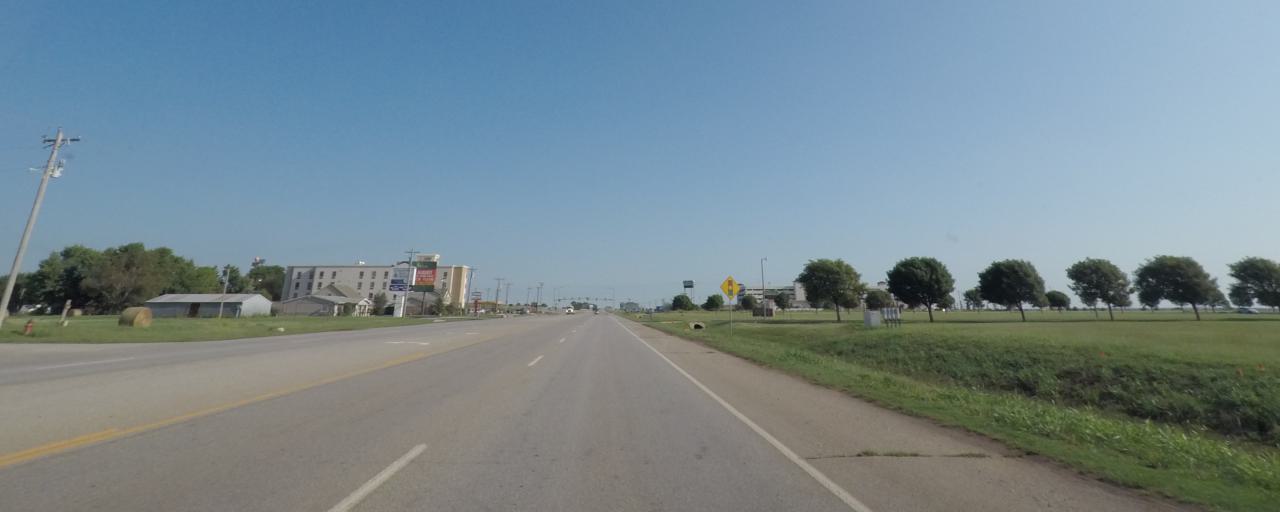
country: US
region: Oklahoma
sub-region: McClain County
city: Newcastle
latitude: 35.2732
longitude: -97.6001
